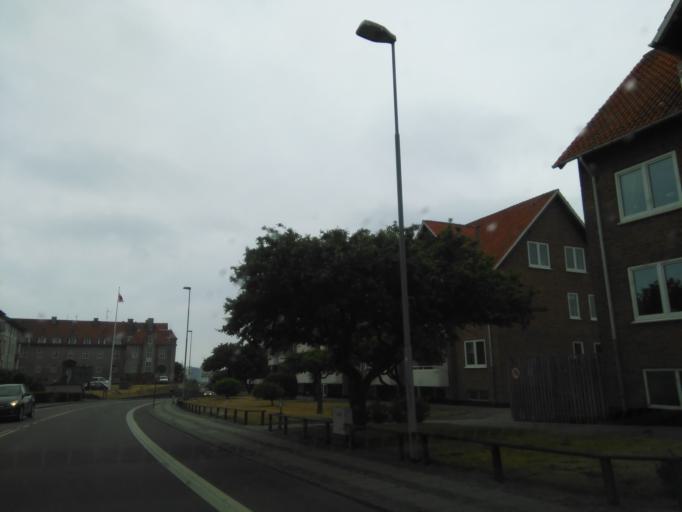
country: DK
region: Capital Region
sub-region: Bornholm Kommune
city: Ronne
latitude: 55.0947
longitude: 14.7022
